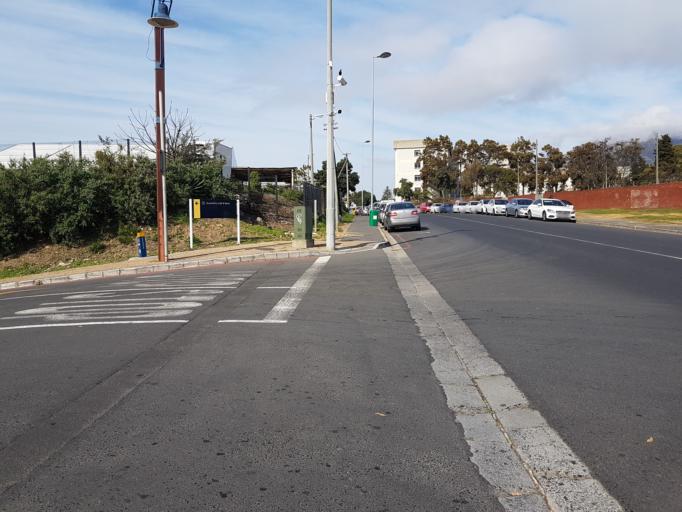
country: ZA
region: Western Cape
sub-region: City of Cape Town
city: Cape Town
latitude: -33.9021
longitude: 18.4143
